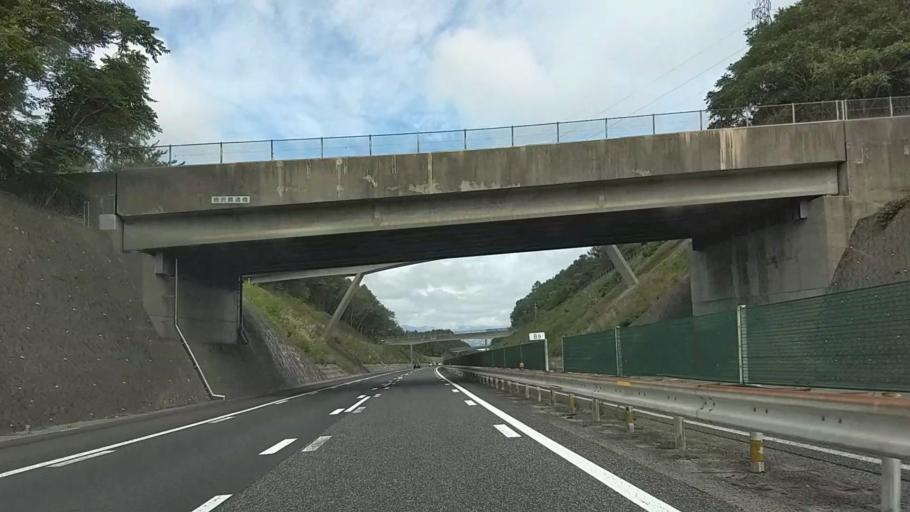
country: JP
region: Nagano
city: Shiojiri
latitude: 36.1026
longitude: 137.9924
